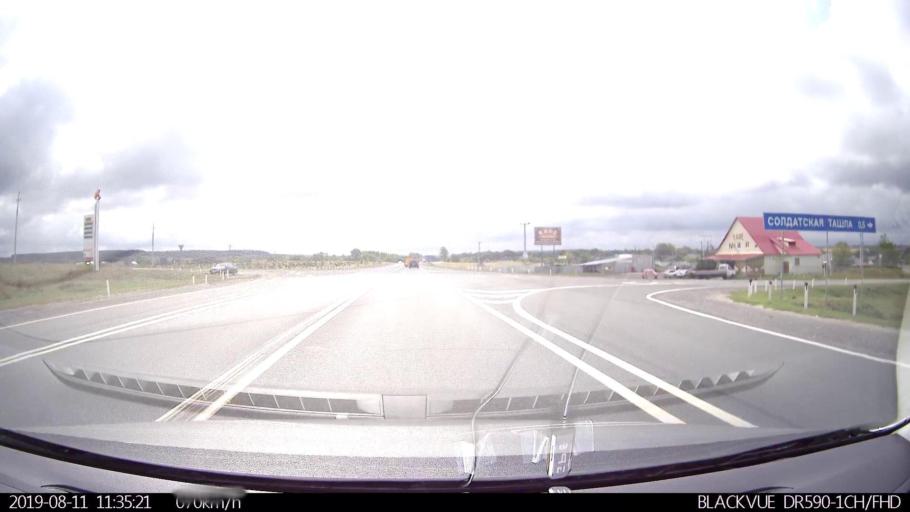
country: RU
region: Ulyanovsk
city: Silikatnyy
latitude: 54.0077
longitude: 48.2189
